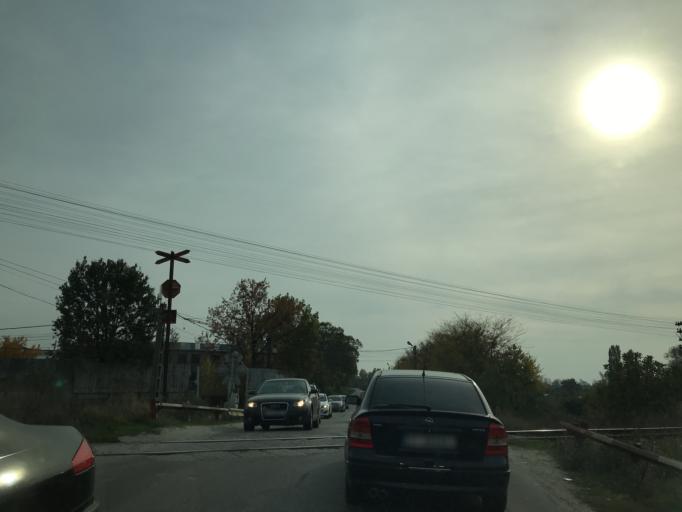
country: RO
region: Olt
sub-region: Comuna Slatioara
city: Slatioara
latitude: 44.3770
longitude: 24.3165
